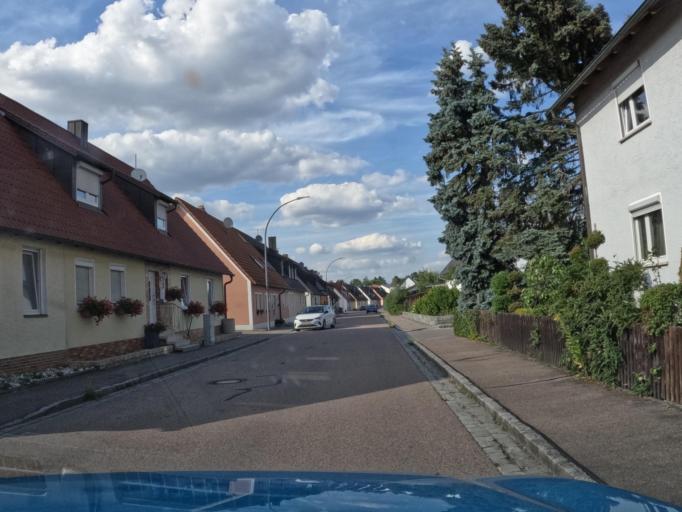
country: DE
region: Bavaria
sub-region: Upper Palatinate
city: Schwarzenfeld
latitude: 49.3845
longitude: 12.1225
